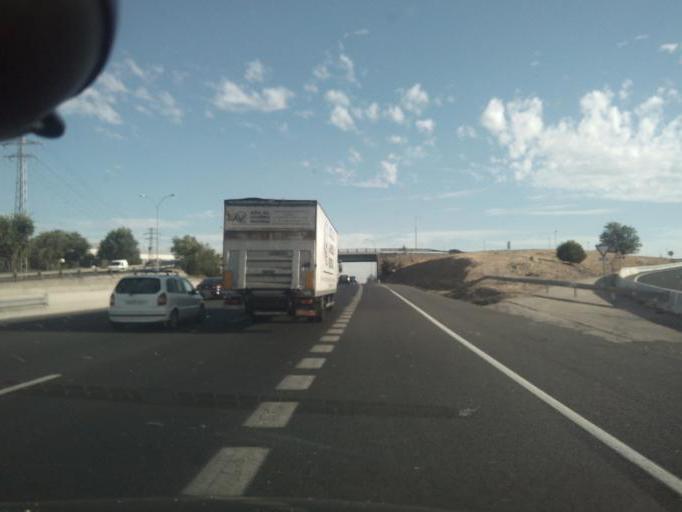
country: ES
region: Madrid
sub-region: Provincia de Madrid
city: Pinto
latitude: 40.2696
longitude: -3.6908
